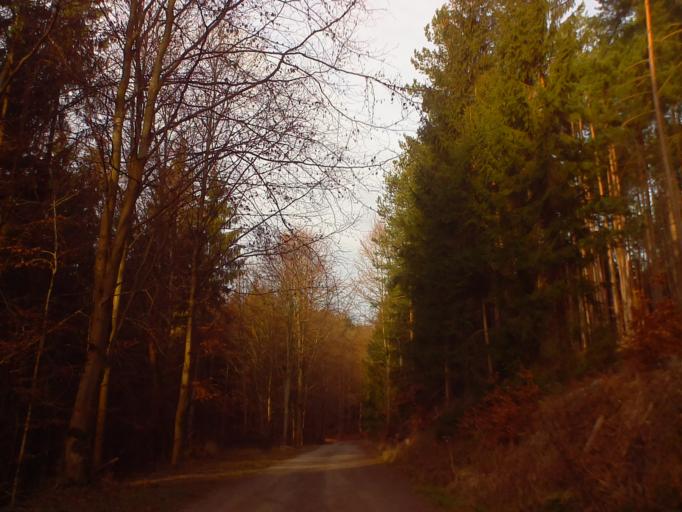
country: DE
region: Thuringia
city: Hummelshain
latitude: 50.7568
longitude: 11.6454
